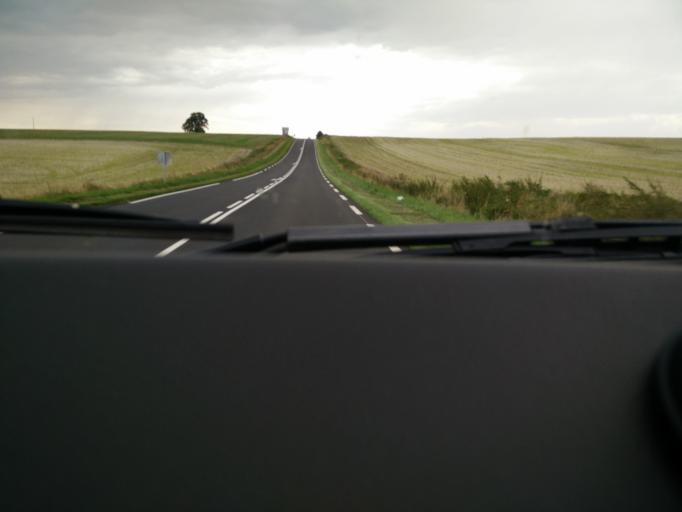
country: FR
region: Picardie
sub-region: Departement de l'Aisne
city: Saint-Michel
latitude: 49.8744
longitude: 4.1677
